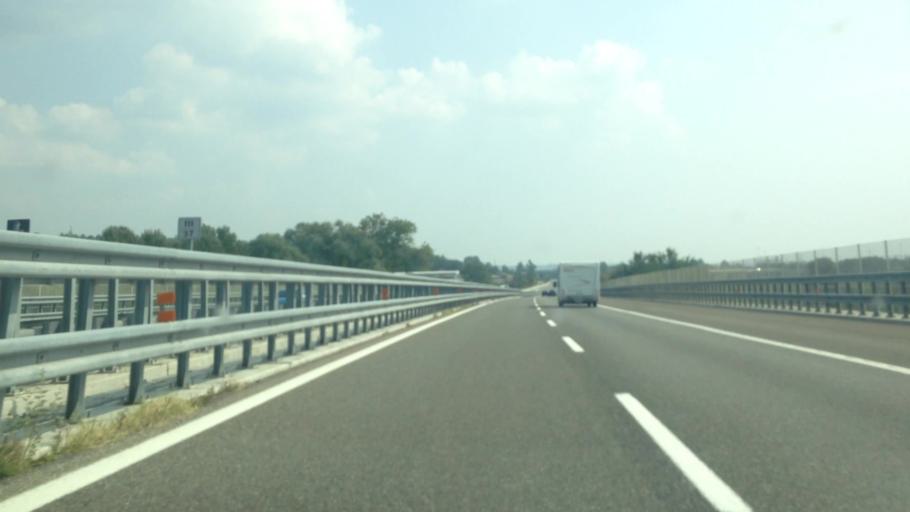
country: IT
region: Piedmont
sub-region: Provincia di Asti
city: Asti
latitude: 44.9137
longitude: 8.2299
